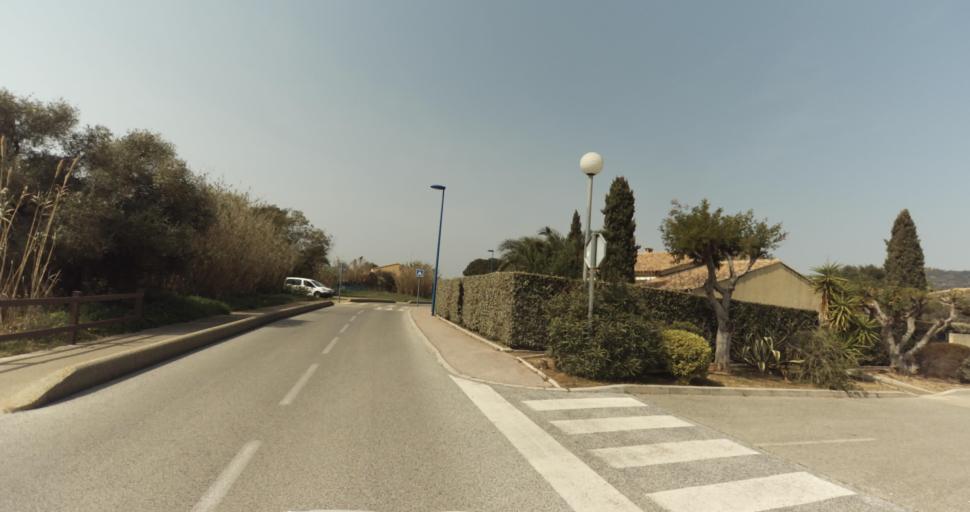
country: FR
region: Provence-Alpes-Cote d'Azur
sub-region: Departement du Var
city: Bormes-les-Mimosas
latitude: 43.1333
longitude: 6.3439
